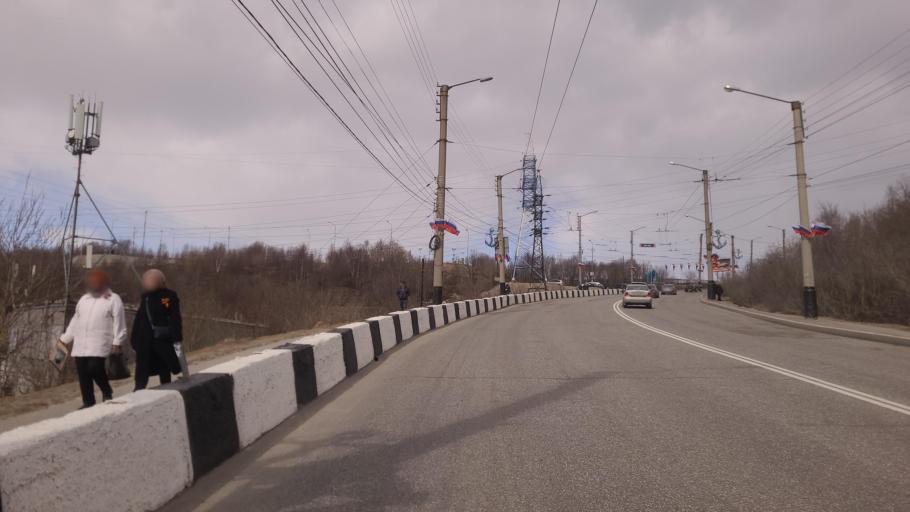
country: RU
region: Murmansk
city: Murmansk
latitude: 68.9861
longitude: 33.0912
